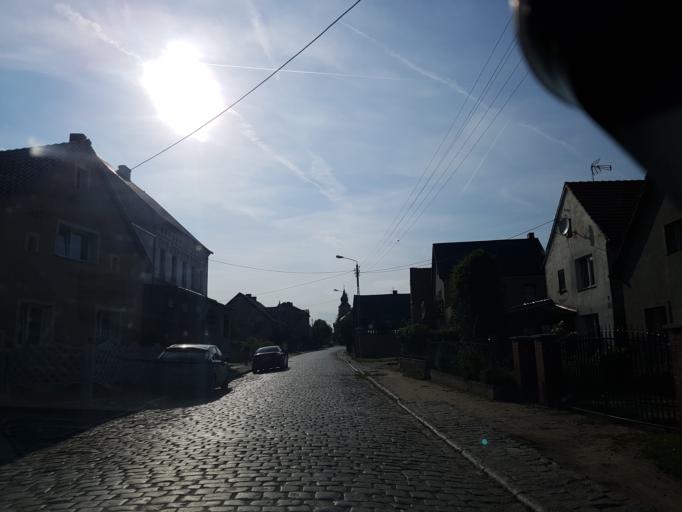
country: PL
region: Lower Silesian Voivodeship
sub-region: Powiat strzelinski
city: Wiazow
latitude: 50.8422
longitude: 17.2130
